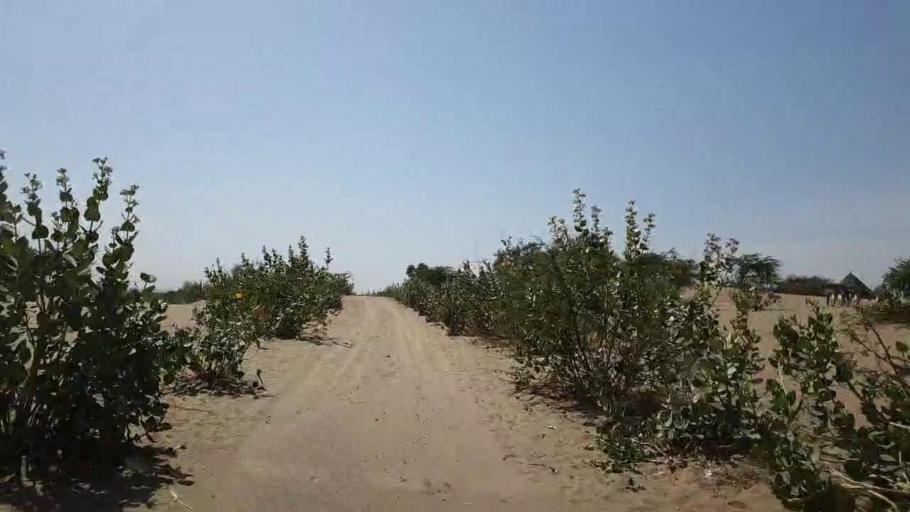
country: PK
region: Sindh
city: Umarkot
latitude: 25.2176
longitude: 69.8740
